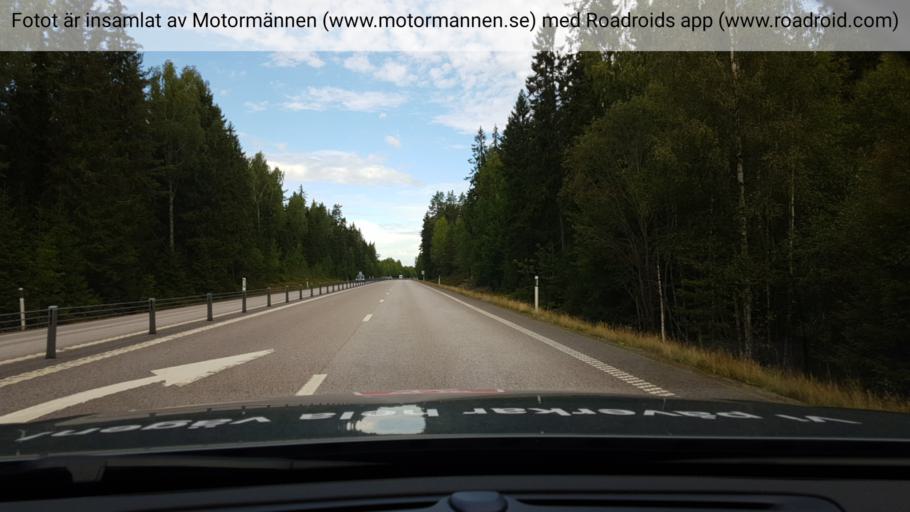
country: SE
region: Uppsala
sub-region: Heby Kommun
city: Tarnsjo
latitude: 60.2693
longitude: 16.9385
